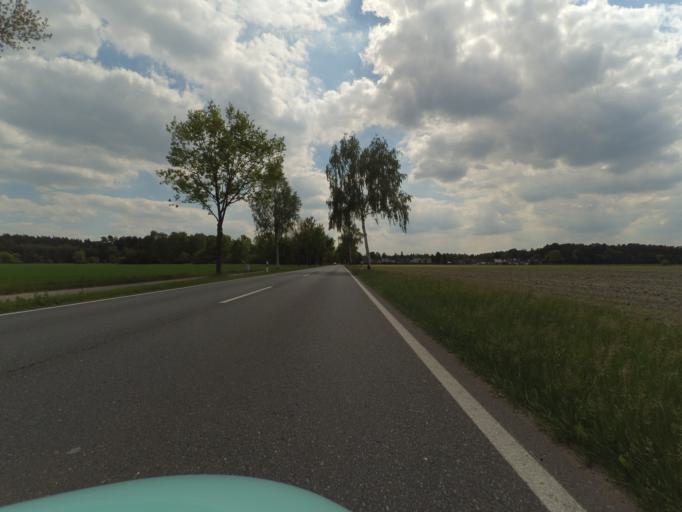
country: DE
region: Lower Saxony
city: Winsen
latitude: 52.6476
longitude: 9.9329
